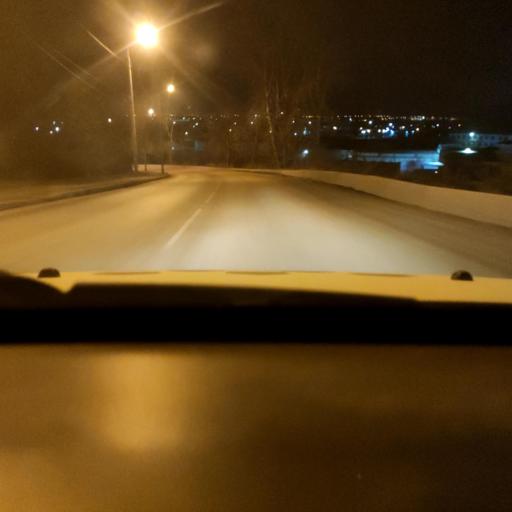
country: RU
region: Perm
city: Perm
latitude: 58.0705
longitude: 56.3529
